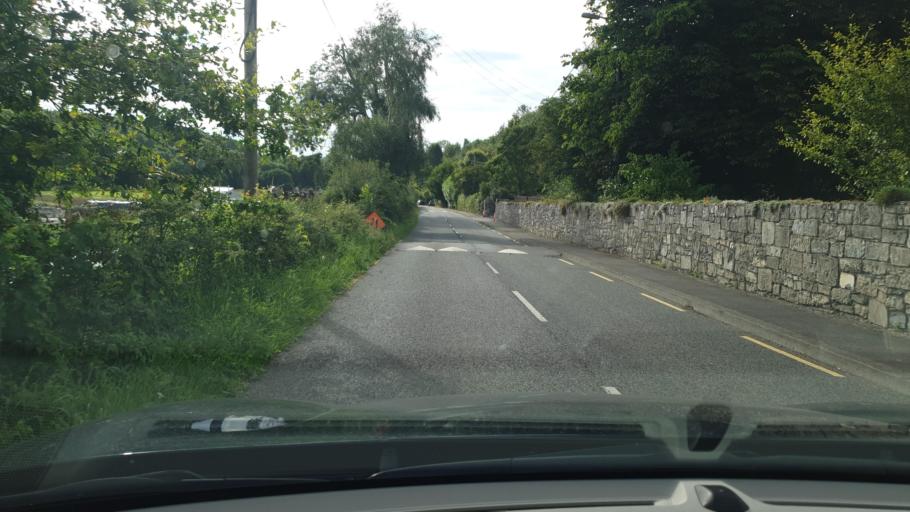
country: IE
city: Palmerstown
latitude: 53.3620
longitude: -6.3961
